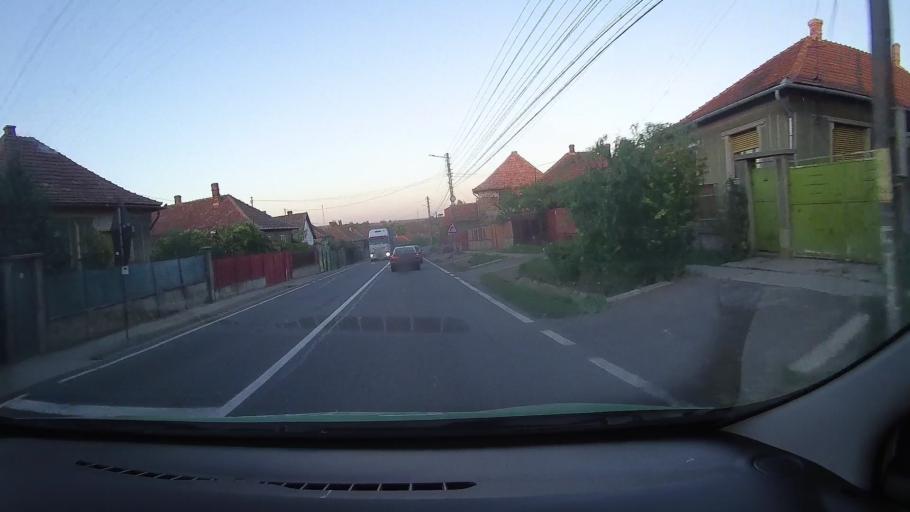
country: RO
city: Szekelyhid
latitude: 47.3544
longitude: 22.1090
